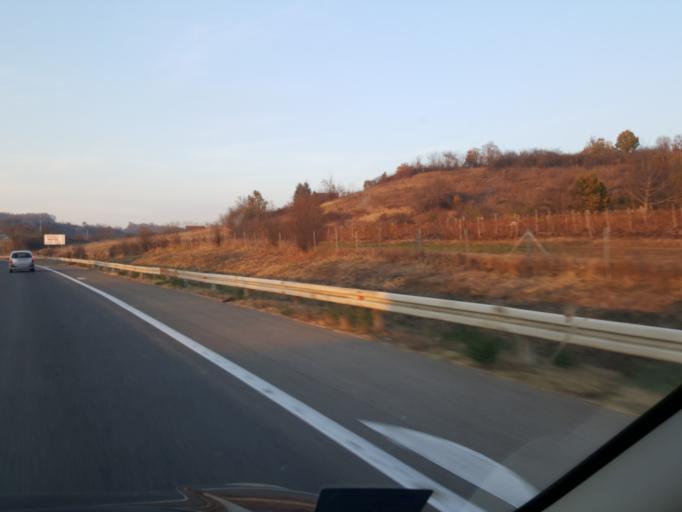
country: RS
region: Central Serbia
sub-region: Nisavski Okrug
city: Aleksinac
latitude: 43.4494
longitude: 21.7985
